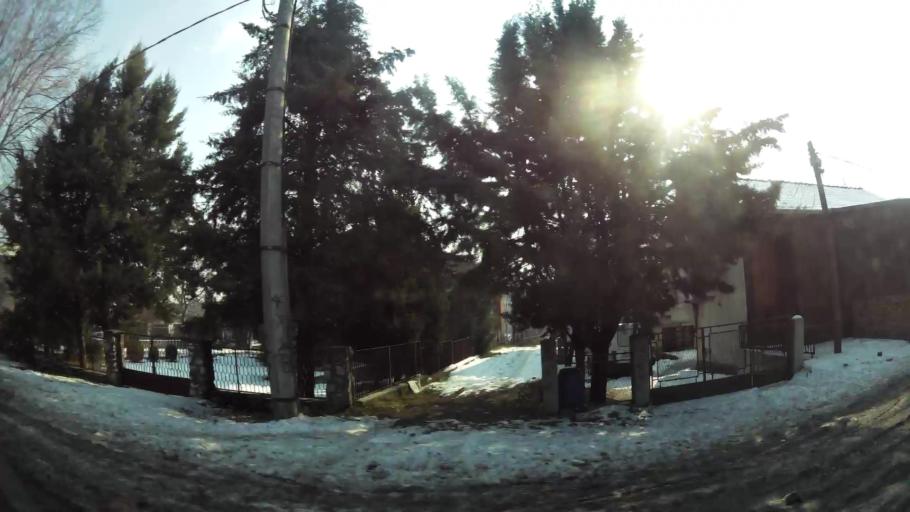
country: MK
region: Suto Orizari
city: Suto Orizare
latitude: 42.0140
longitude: 21.3921
